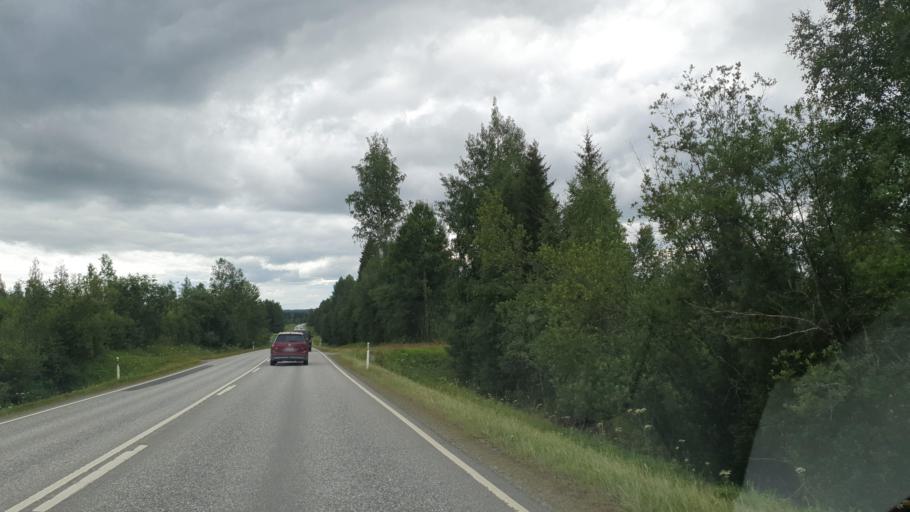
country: FI
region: Northern Savo
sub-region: Ylae-Savo
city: Sonkajaervi
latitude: 63.7374
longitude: 27.3793
